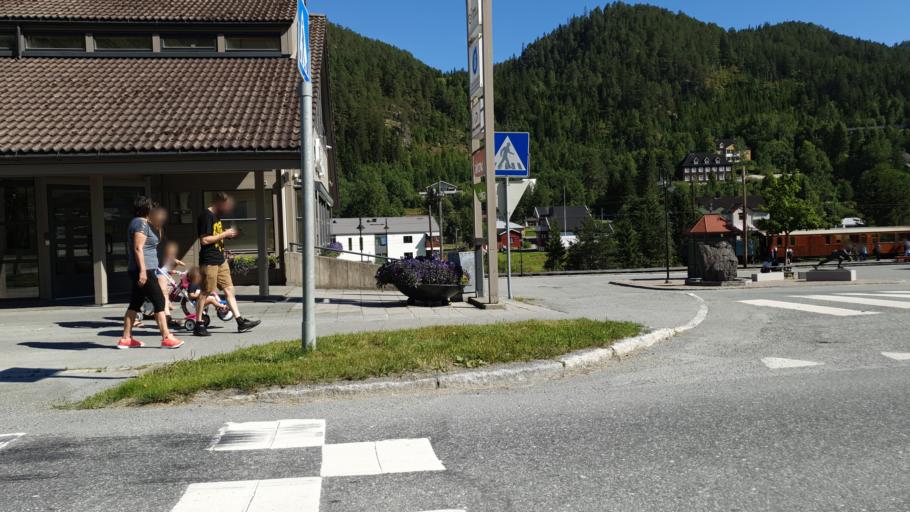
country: NO
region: Sor-Trondelag
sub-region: Meldal
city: Meldal
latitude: 63.1260
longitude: 9.7047
